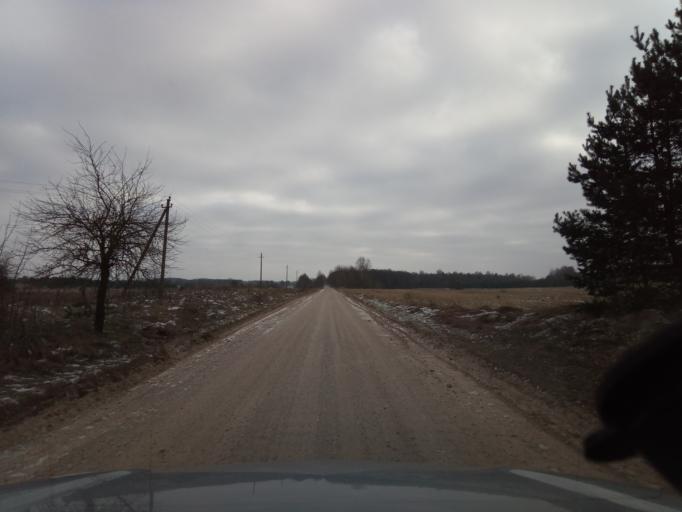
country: LT
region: Alytaus apskritis
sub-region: Alytaus rajonas
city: Daugai
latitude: 54.3224
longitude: 24.3234
